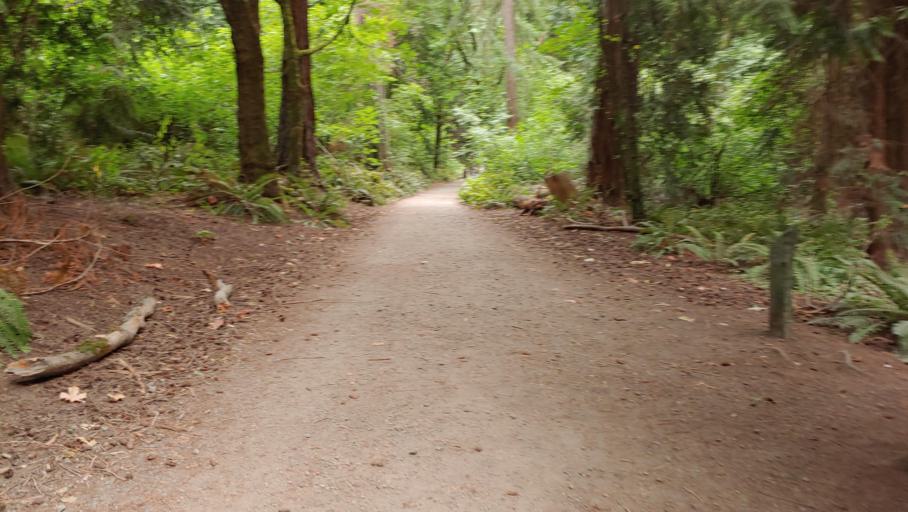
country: US
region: Washington
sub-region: King County
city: Mercer Island
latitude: 47.5564
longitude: -122.2514
